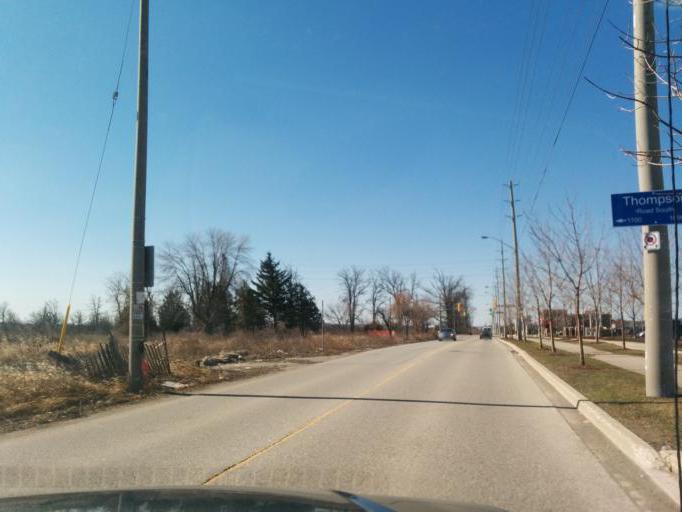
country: CA
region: Ontario
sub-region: Halton
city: Milton
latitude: 43.5075
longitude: -79.8366
